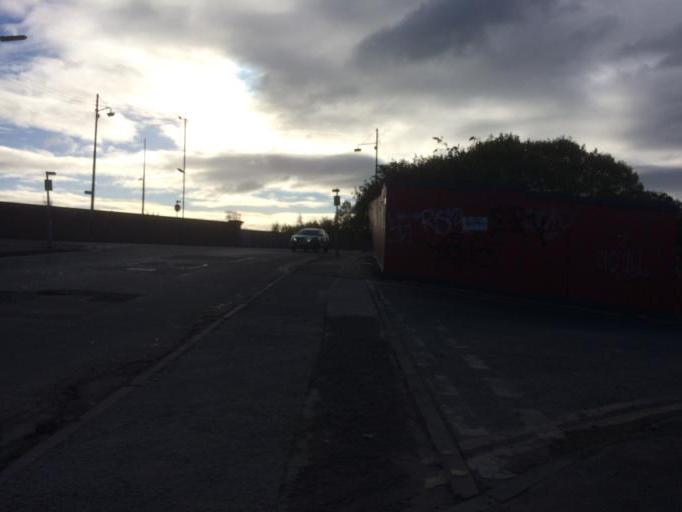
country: GB
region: Scotland
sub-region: Glasgow City
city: Glasgow
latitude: 55.8583
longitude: -4.2322
